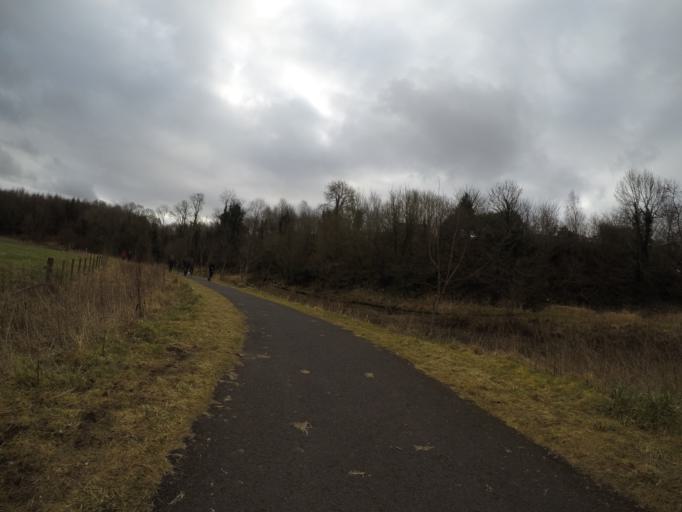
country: GB
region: Scotland
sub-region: North Ayrshire
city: Springside
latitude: 55.6128
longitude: -4.6115
